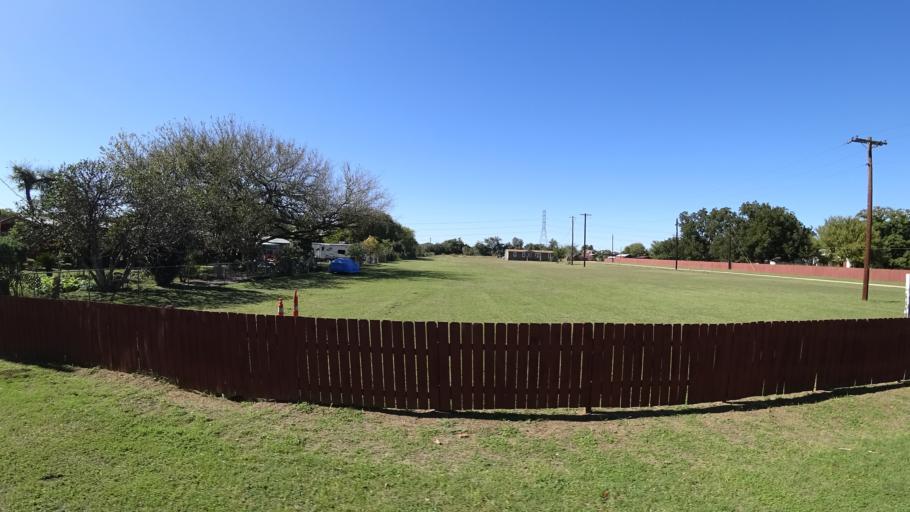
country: US
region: Texas
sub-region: Travis County
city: Hornsby Bend
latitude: 30.2758
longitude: -97.6479
